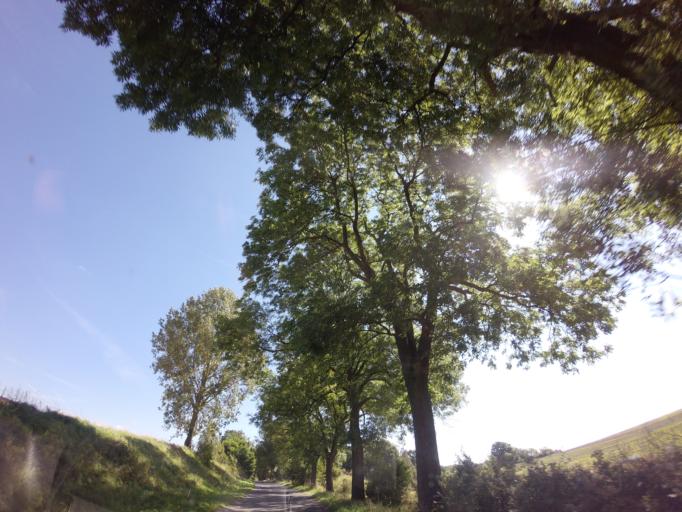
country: PL
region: West Pomeranian Voivodeship
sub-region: Powiat choszczenski
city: Krzecin
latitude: 53.1558
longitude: 15.5225
